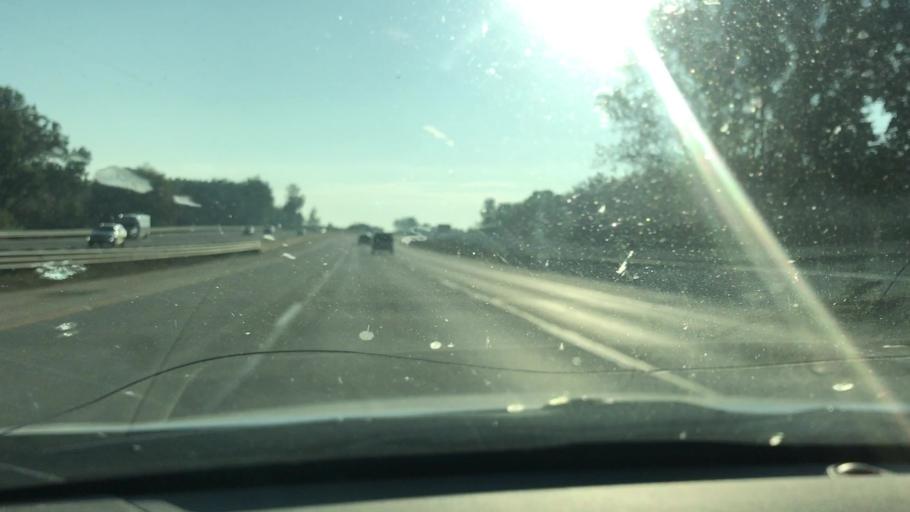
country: US
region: Michigan
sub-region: Livingston County
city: Howell
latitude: 42.5844
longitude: -83.9145
